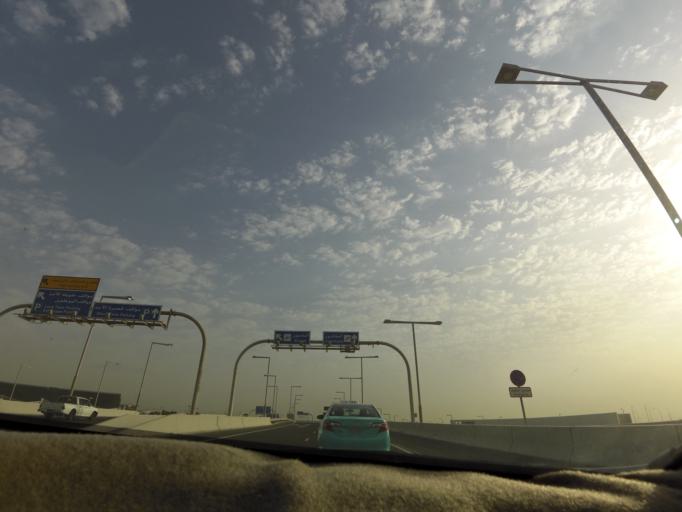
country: QA
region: Al Wakrah
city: Al Wakrah
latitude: 25.2567
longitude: 51.6169
